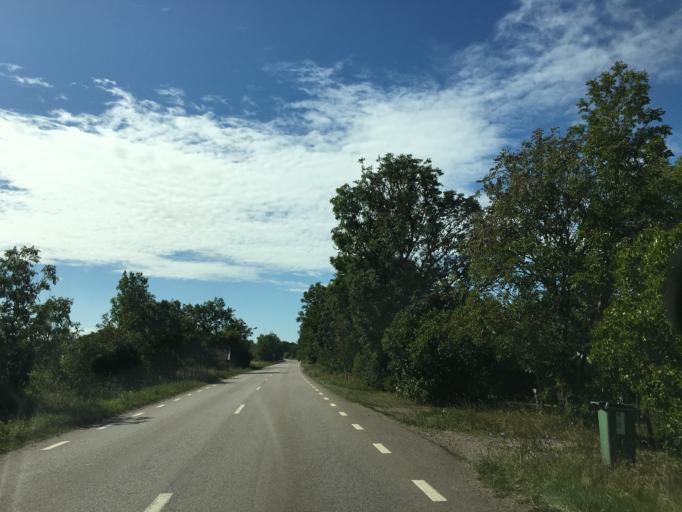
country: SE
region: Kalmar
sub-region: Morbylanga Kommun
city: Moerbylanga
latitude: 56.5210
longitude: 16.4401
